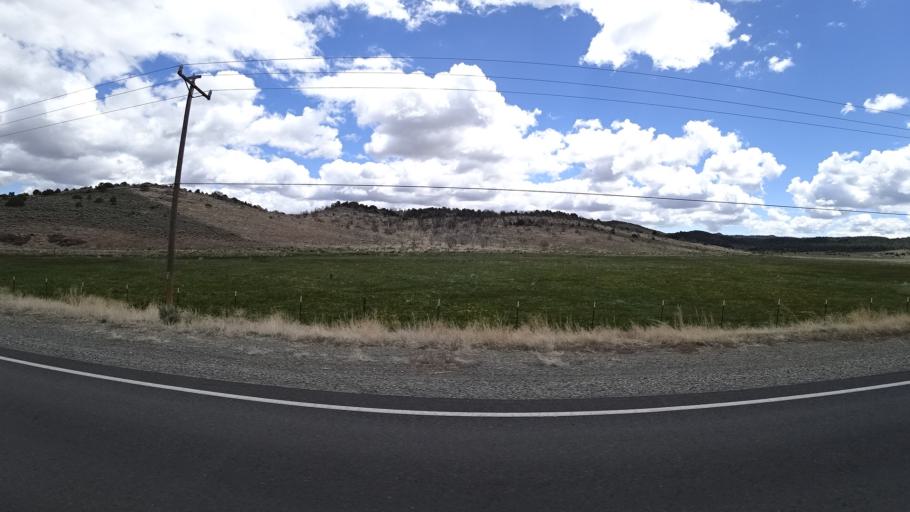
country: US
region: California
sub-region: Mono County
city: Bridgeport
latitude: 38.2220
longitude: -119.2286
